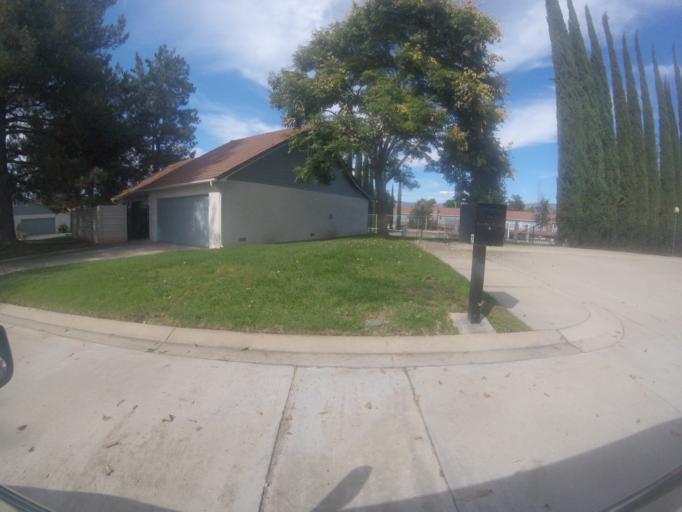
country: US
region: California
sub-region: San Bernardino County
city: Mentone
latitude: 34.0544
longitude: -117.1486
